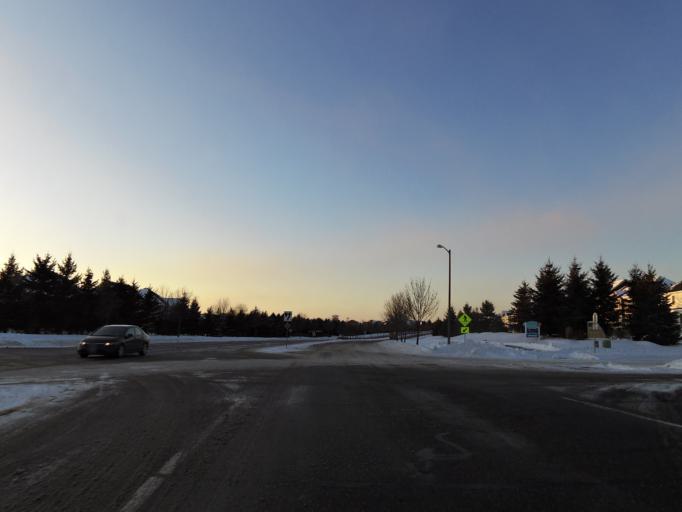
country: US
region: Minnesota
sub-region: Washington County
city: Lake Elmo
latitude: 44.9231
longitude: -92.8792
